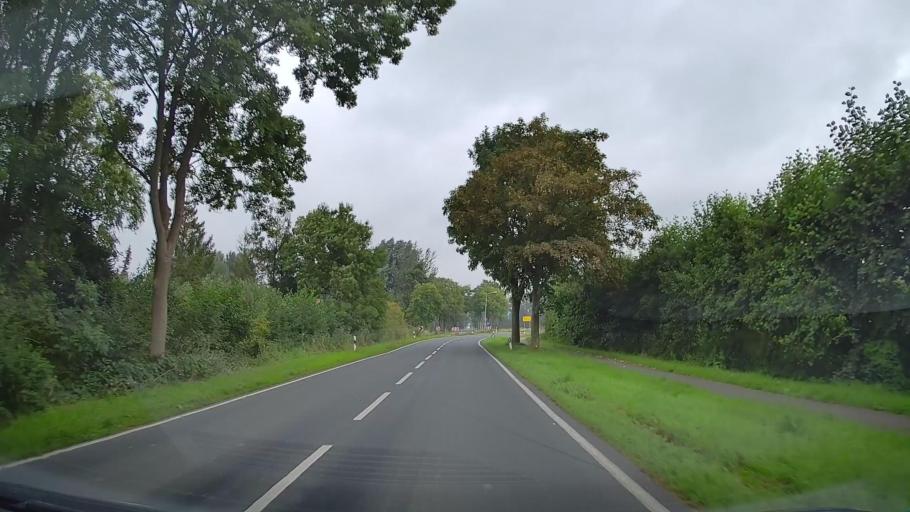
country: DE
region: Lower Saxony
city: Balje
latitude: 53.8210
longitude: 9.1318
